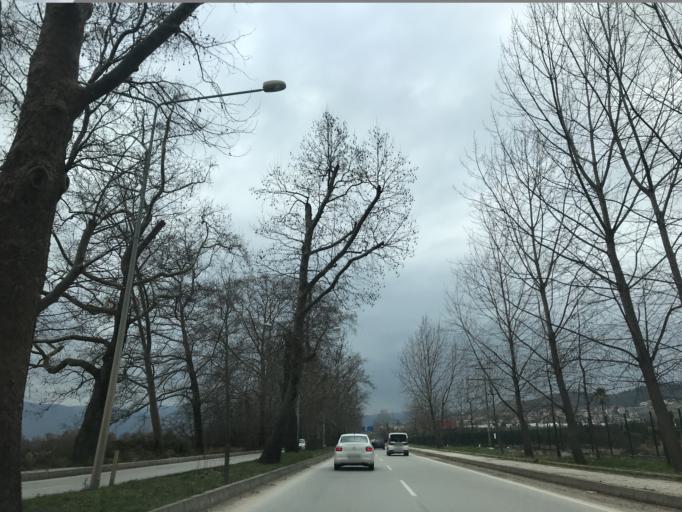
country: TR
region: Yalova
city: Kadikoy
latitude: 40.6492
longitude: 29.2390
